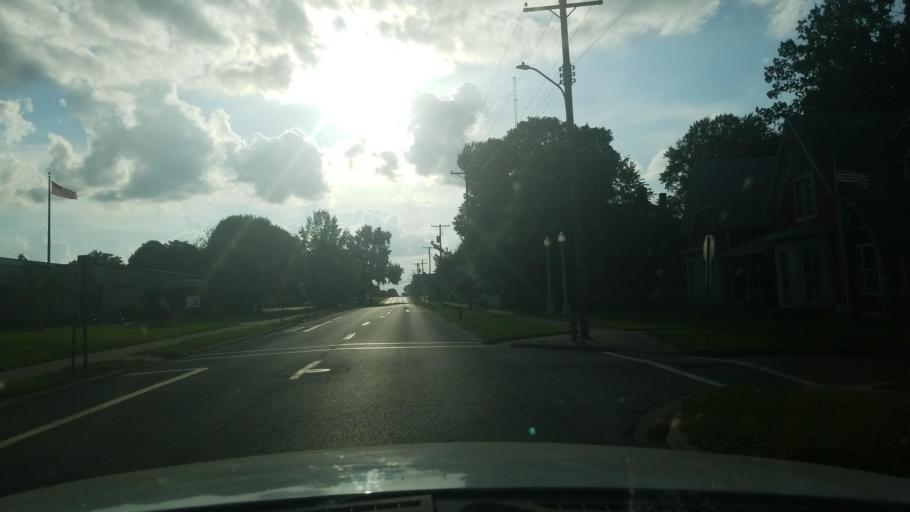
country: US
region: Illinois
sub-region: Saline County
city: Harrisburg
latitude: 37.7341
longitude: -88.5354
